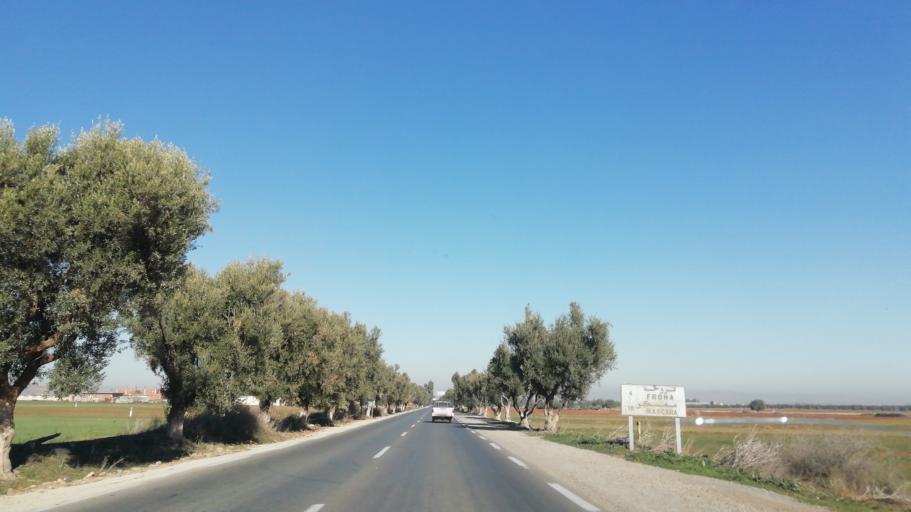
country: DZ
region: Mascara
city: Mascara
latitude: 35.2701
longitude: 0.1287
